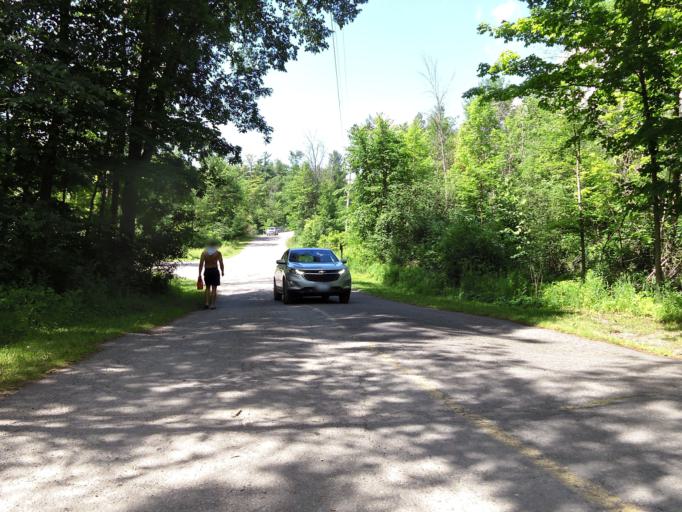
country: CA
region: Ontario
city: Arnprior
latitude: 45.4827
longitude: -76.2206
